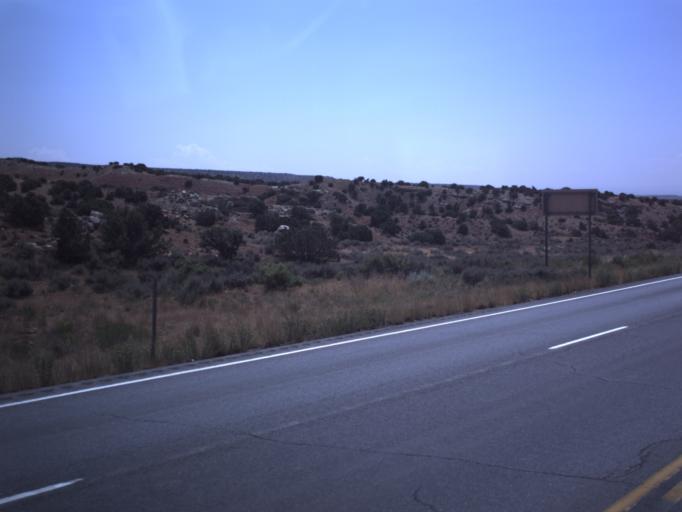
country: US
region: Utah
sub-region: Uintah County
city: Maeser
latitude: 40.4039
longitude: -109.5910
